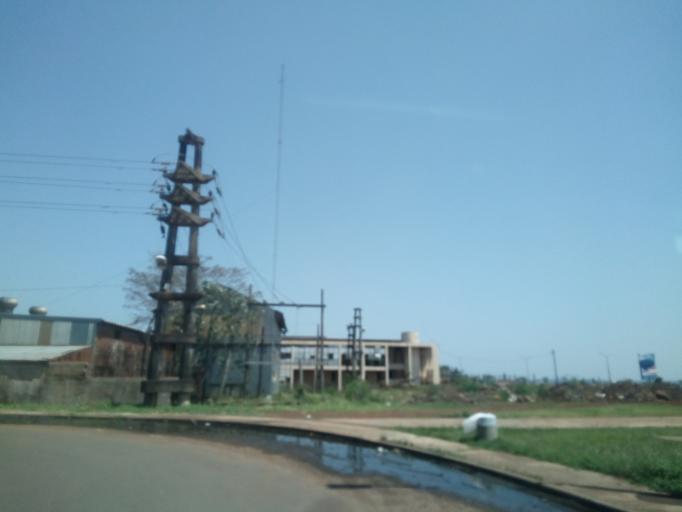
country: AR
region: Misiones
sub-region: Departamento de Capital
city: Posadas
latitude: -27.3570
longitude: -55.9055
